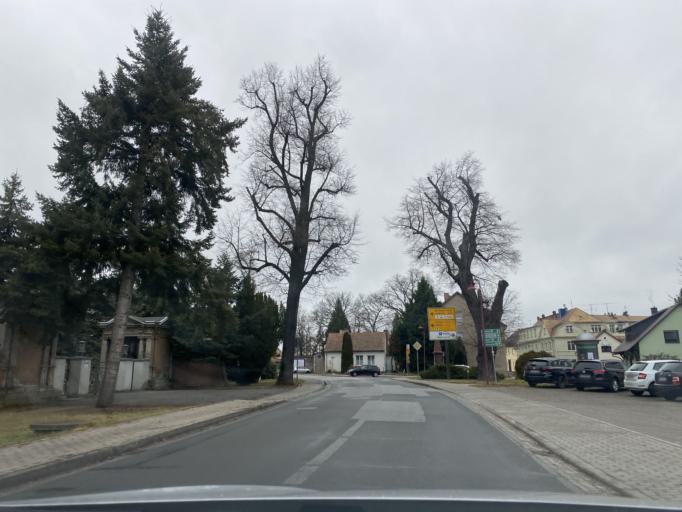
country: DE
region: Saxony
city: Rothenburg
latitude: 51.3313
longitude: 14.9704
